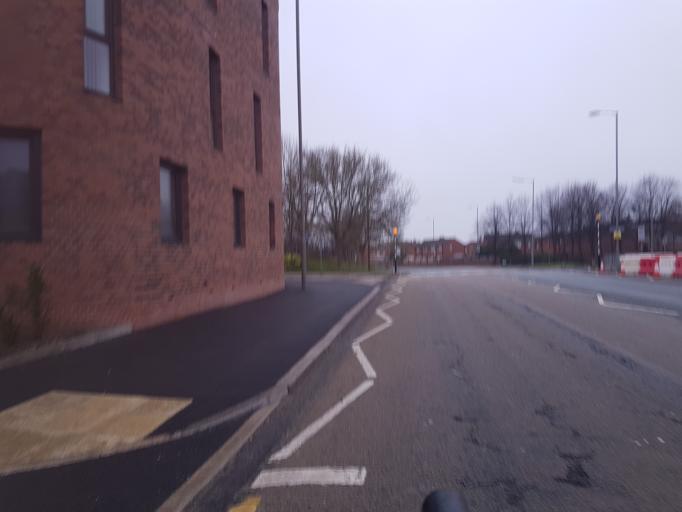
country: GB
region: England
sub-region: Liverpool
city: Liverpool
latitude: 53.4313
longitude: -2.9784
